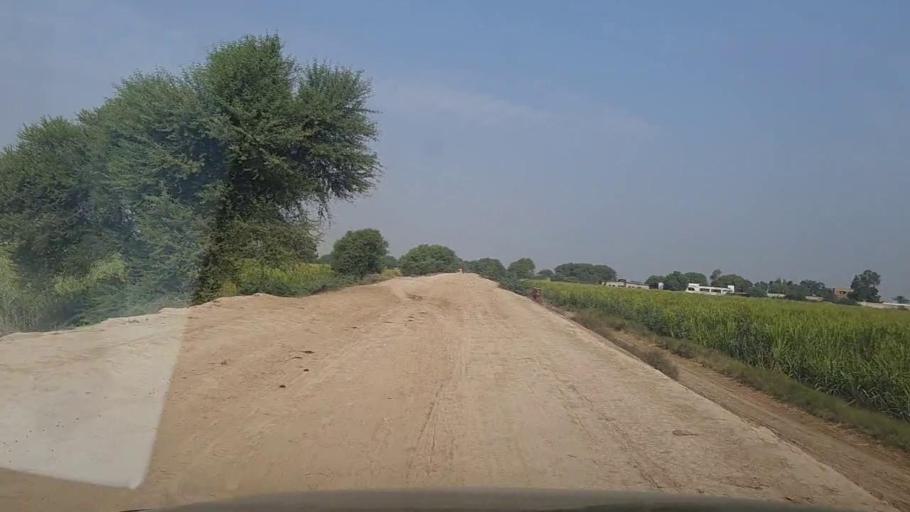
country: PK
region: Sindh
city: Bulri
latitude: 25.0220
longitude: 68.2826
